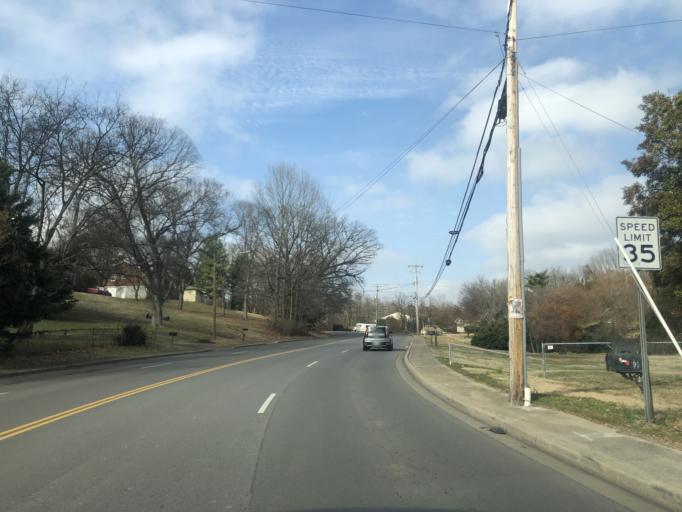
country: US
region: Tennessee
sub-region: Davidson County
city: Oak Hill
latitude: 36.0994
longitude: -86.7178
